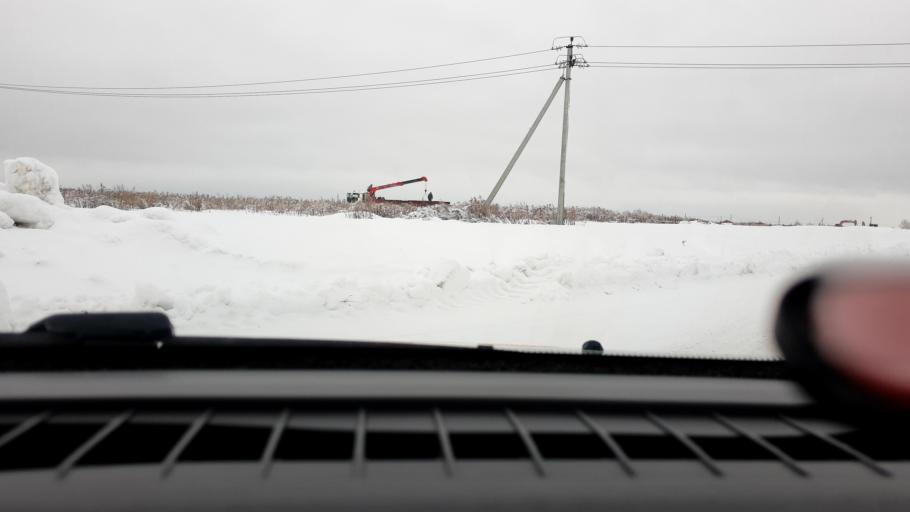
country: RU
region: Nizjnij Novgorod
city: Afonino
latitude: 56.2011
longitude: 44.0680
